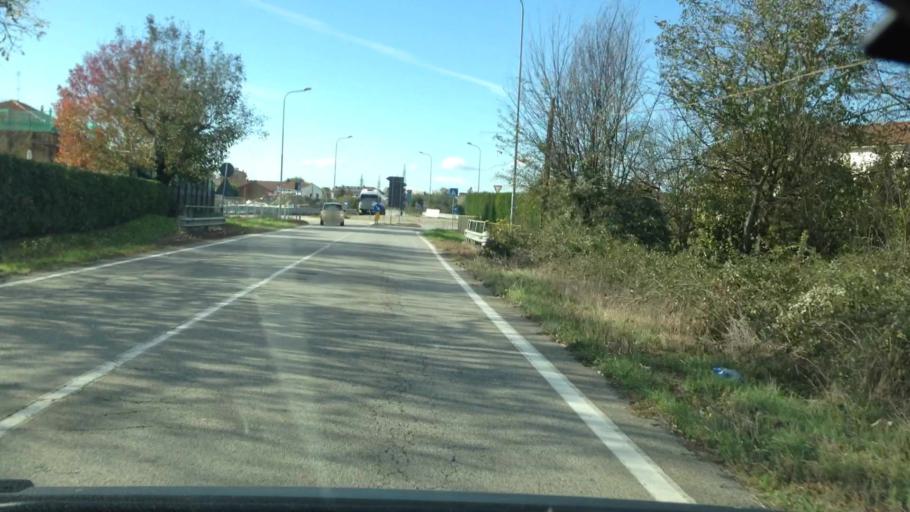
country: IT
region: Piedmont
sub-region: Provincia di Alessandria
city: Felizzano
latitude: 44.9007
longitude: 8.4399
